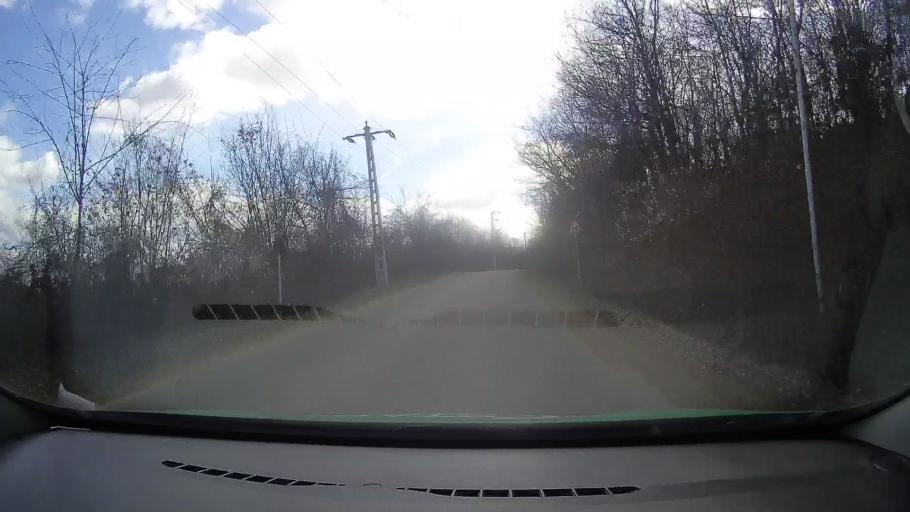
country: RO
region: Dambovita
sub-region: Comuna Sotanga
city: Teis
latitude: 44.9703
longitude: 25.3959
